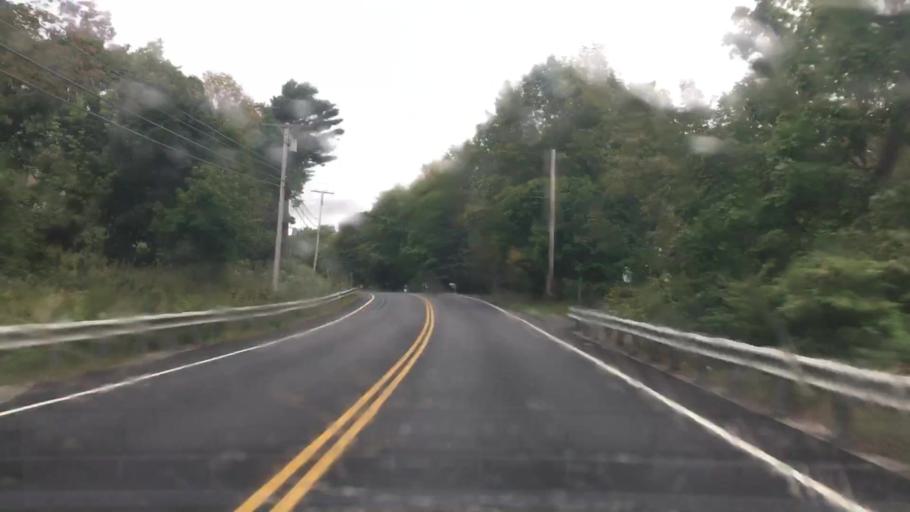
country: US
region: Maine
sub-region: Penobscot County
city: Orrington
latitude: 44.6842
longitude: -68.8105
